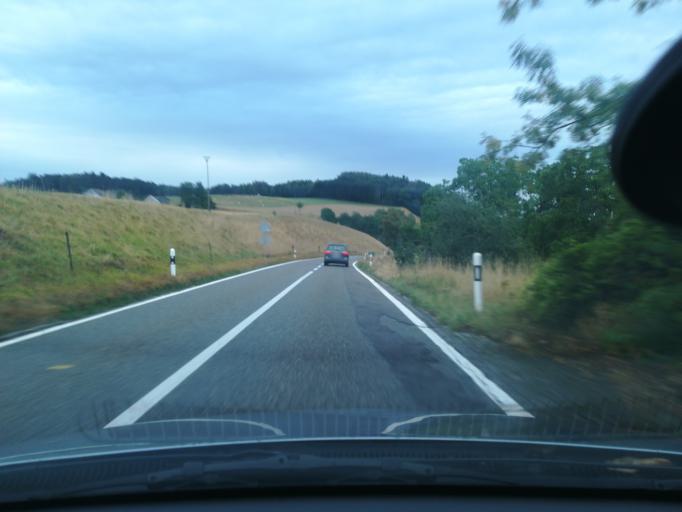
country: CH
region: Thurgau
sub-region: Frauenfeld District
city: Huttwilen
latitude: 47.6138
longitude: 8.8856
